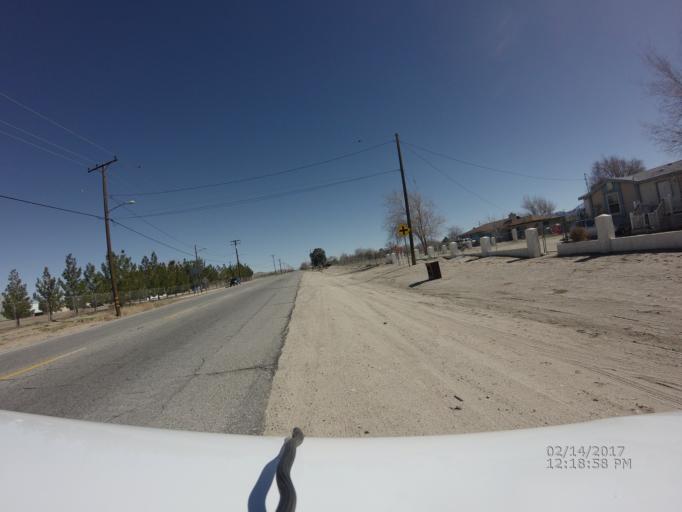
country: US
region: California
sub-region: Los Angeles County
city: Littlerock
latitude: 34.5798
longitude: -117.9533
